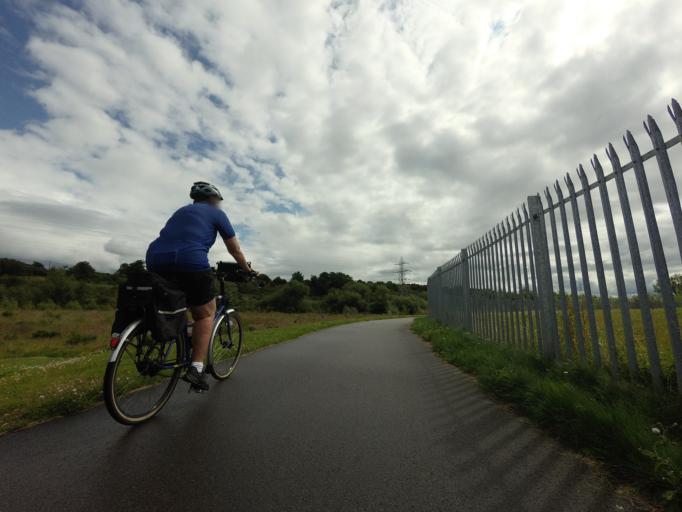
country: GB
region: Scotland
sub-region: Moray
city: Elgin
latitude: 57.6527
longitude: -3.2932
